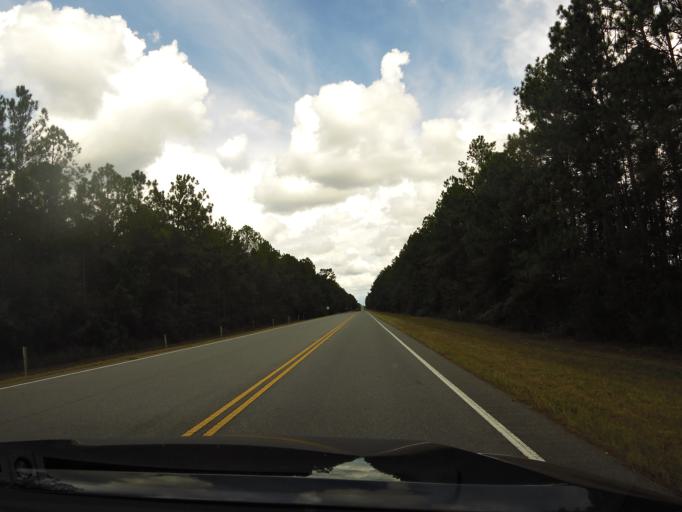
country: US
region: Georgia
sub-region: Brantley County
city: Nahunta
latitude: 31.0205
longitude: -82.0241
